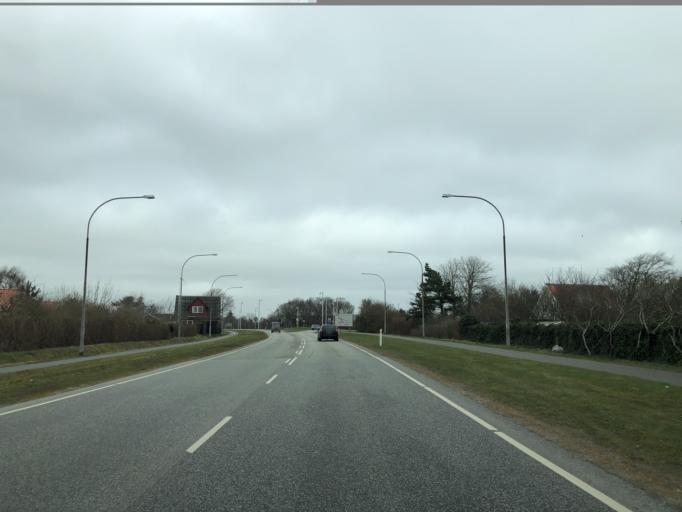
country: DK
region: North Denmark
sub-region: Frederikshavn Kommune
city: Saeby
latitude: 57.3403
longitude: 10.5150
